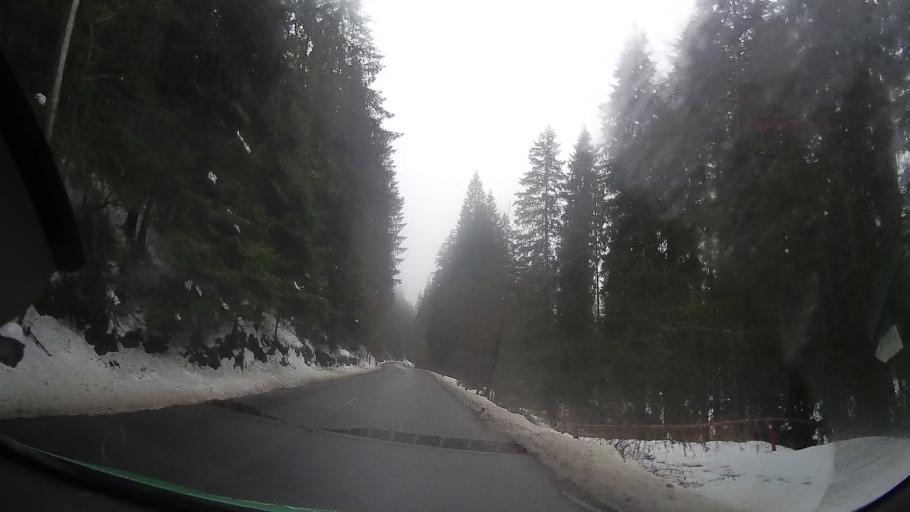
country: RO
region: Neamt
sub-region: Comuna Bicaz Chei
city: Bicaz Chei
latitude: 46.7865
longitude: 25.7876
